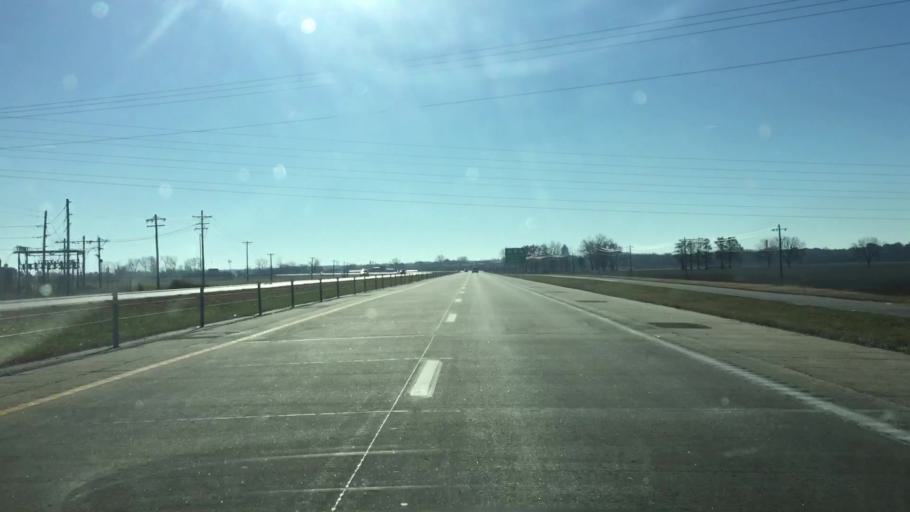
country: US
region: Missouri
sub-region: Cole County
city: Jefferson City
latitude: 38.6129
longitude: -92.1867
